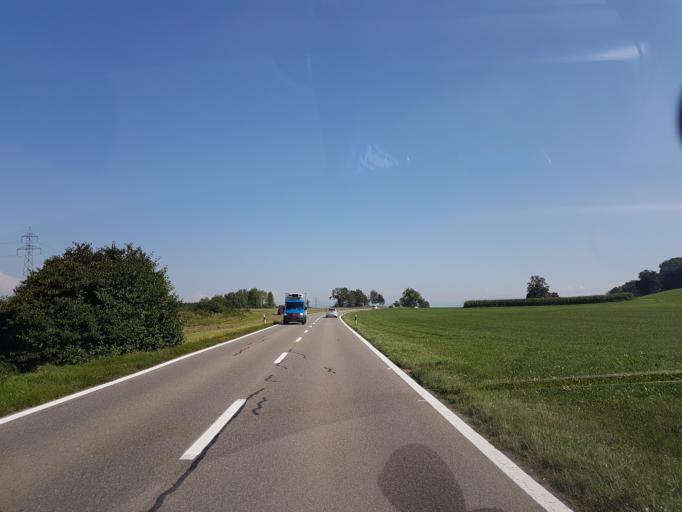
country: CH
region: Aargau
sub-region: Bezirk Muri
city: Waltenschwil
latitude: 47.3249
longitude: 8.2947
